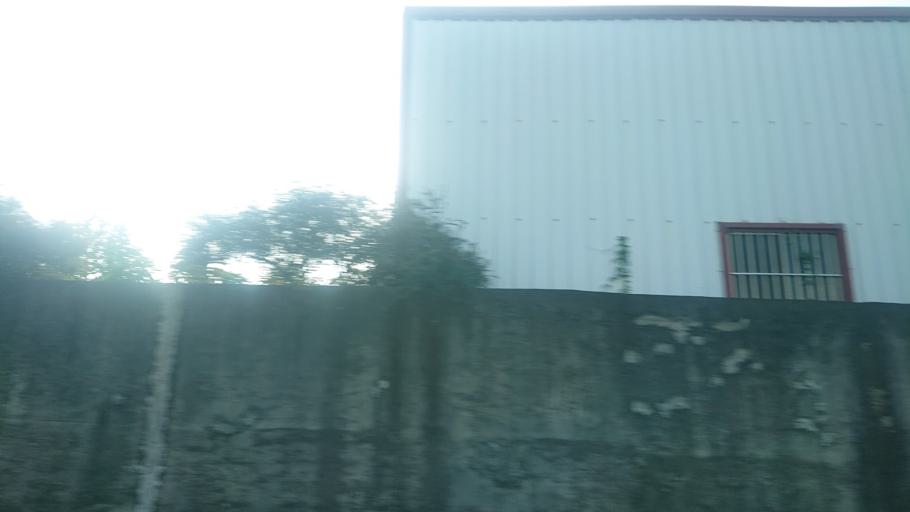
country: TW
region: Taiwan
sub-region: Tainan
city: Tainan
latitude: 23.0743
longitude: 120.2136
